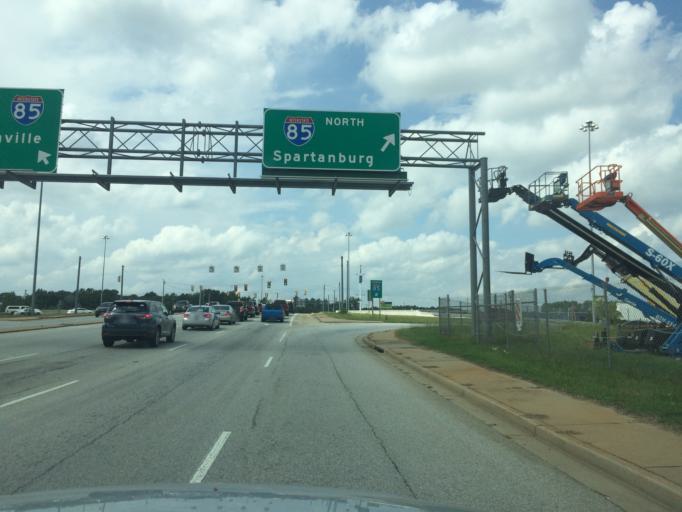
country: US
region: South Carolina
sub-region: Greenville County
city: Five Forks
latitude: 34.8705
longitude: -82.2234
